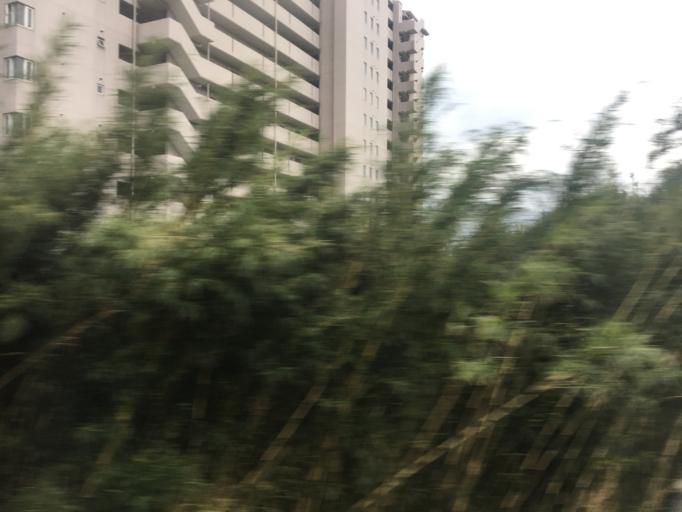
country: JP
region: Chiba
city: Tateyama
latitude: 35.0952
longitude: 139.8494
